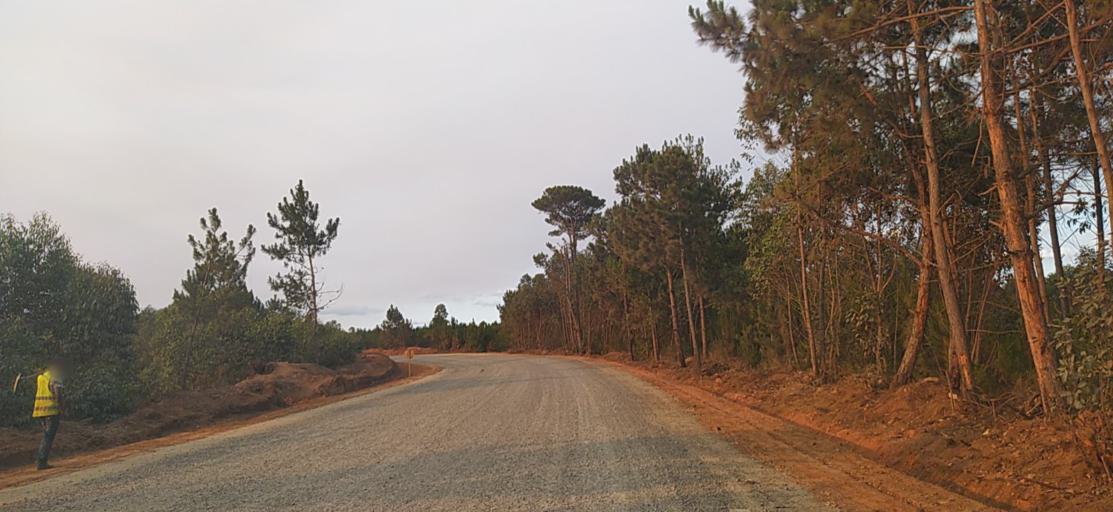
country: MG
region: Alaotra Mangoro
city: Moramanga
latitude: -18.5462
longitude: 48.2599
